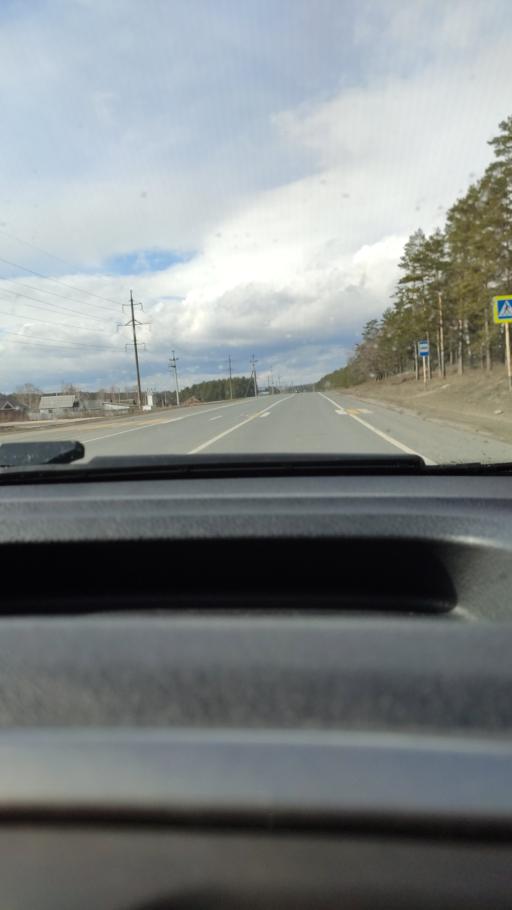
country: RU
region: Samara
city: Volzhskiy
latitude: 53.4609
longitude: 50.0799
